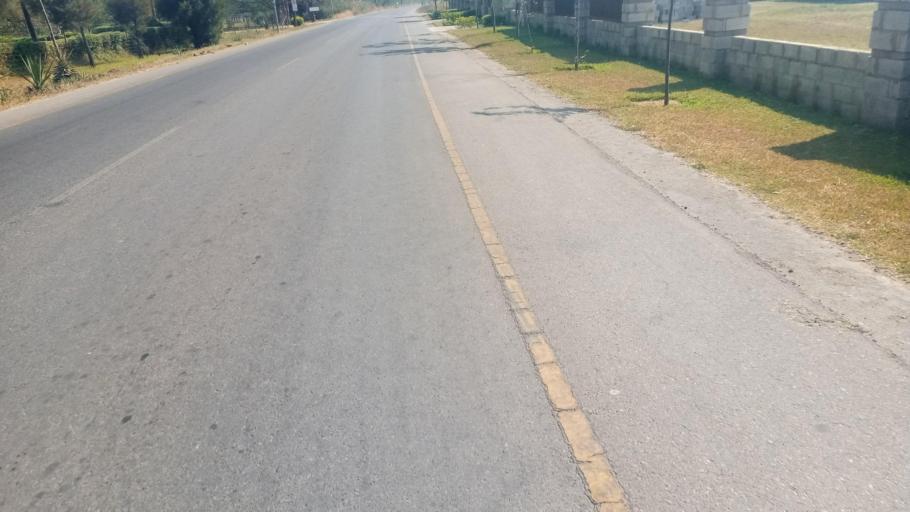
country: ZM
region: Lusaka
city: Lusaka
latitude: -15.4554
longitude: 28.4343
